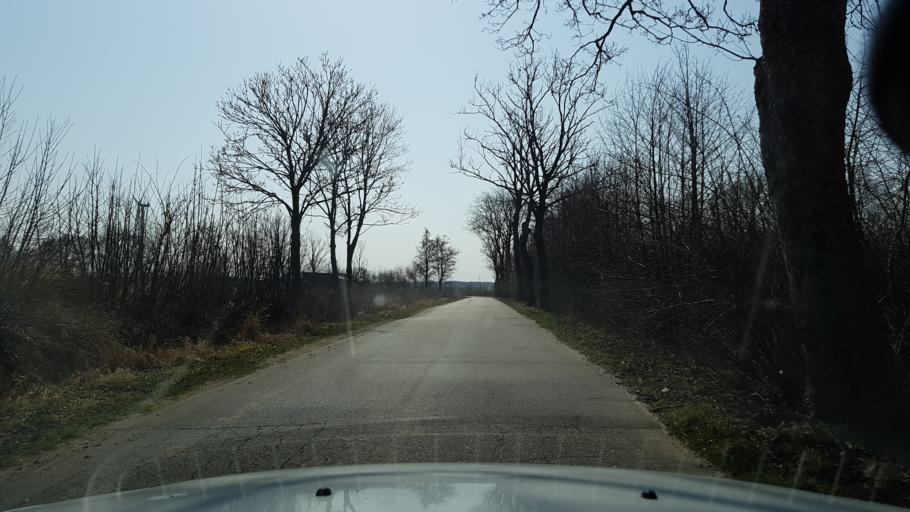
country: PL
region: West Pomeranian Voivodeship
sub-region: Powiat slawienski
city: Darlowo
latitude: 54.4980
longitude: 16.5042
